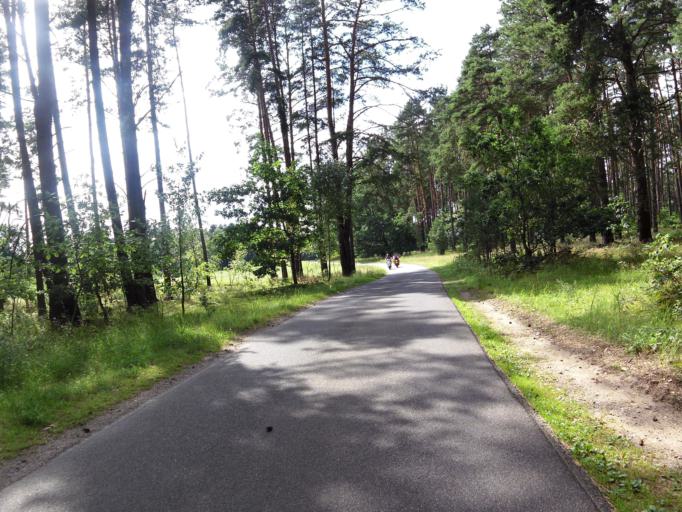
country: DE
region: Brandenburg
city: Lychen
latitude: 53.2869
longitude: 13.3197
